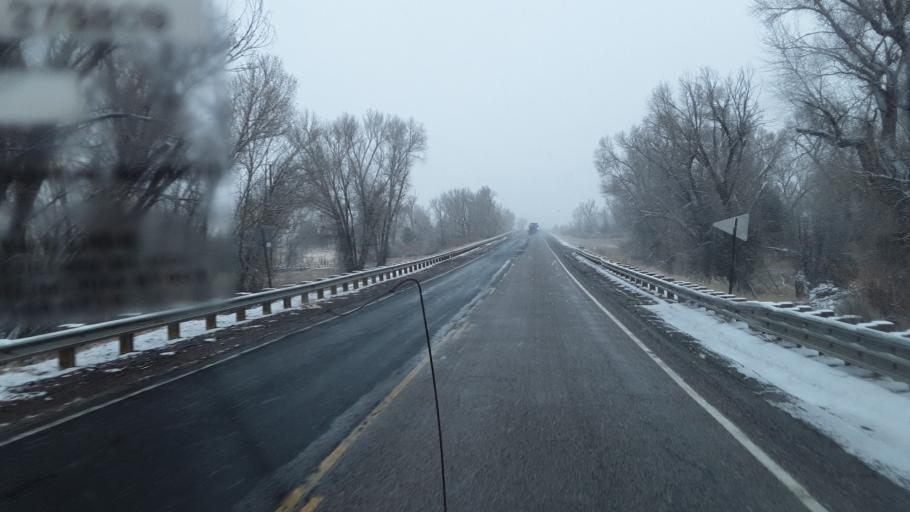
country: US
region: New Mexico
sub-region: Rio Arriba County
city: Chama
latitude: 36.8093
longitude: -106.5678
